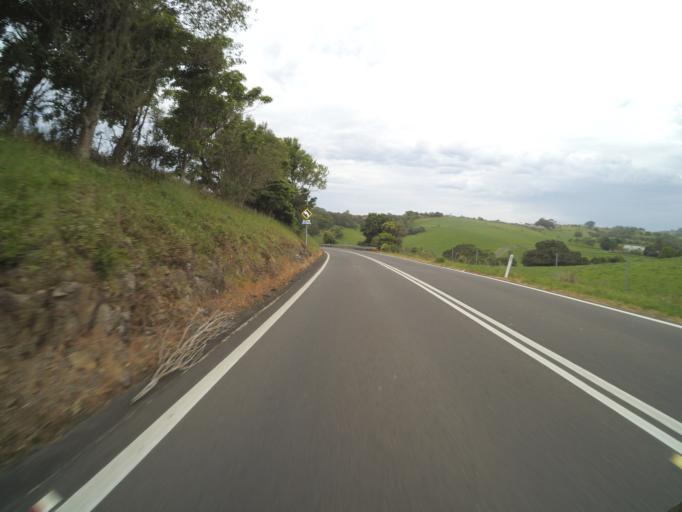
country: AU
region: New South Wales
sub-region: Kiama
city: Kiama
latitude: -34.6650
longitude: 150.8351
